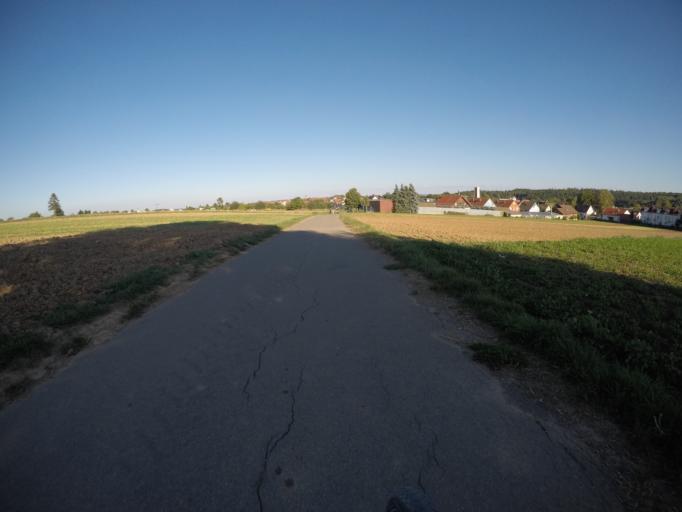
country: DE
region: Baden-Wuerttemberg
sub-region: Regierungsbezirk Stuttgart
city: Weil im Schonbuch
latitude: 48.6230
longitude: 9.0439
